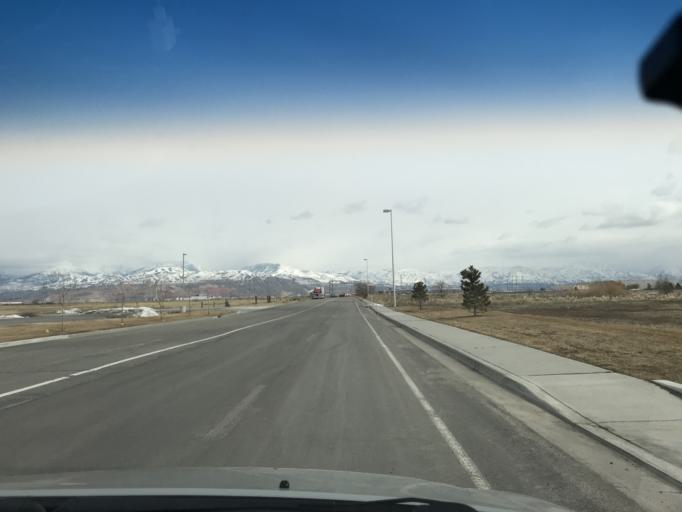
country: US
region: Utah
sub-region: Salt Lake County
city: West Valley City
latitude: 40.7873
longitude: -112.0201
